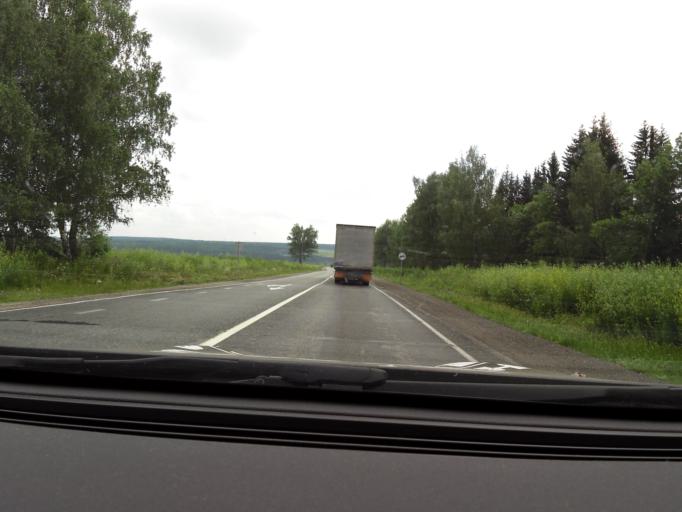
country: RU
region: Perm
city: Suksun
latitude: 57.0739
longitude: 57.4118
